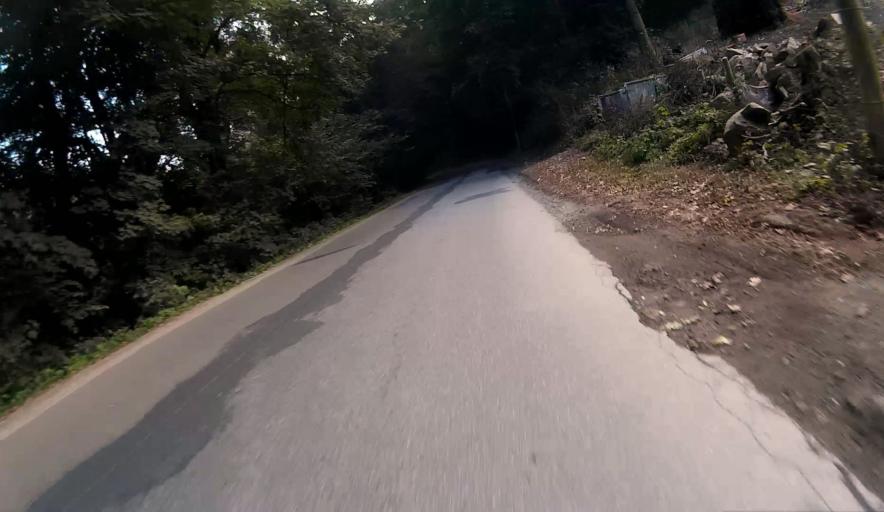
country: CZ
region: South Moravian
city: Podoli
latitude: 49.1974
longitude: 16.7171
